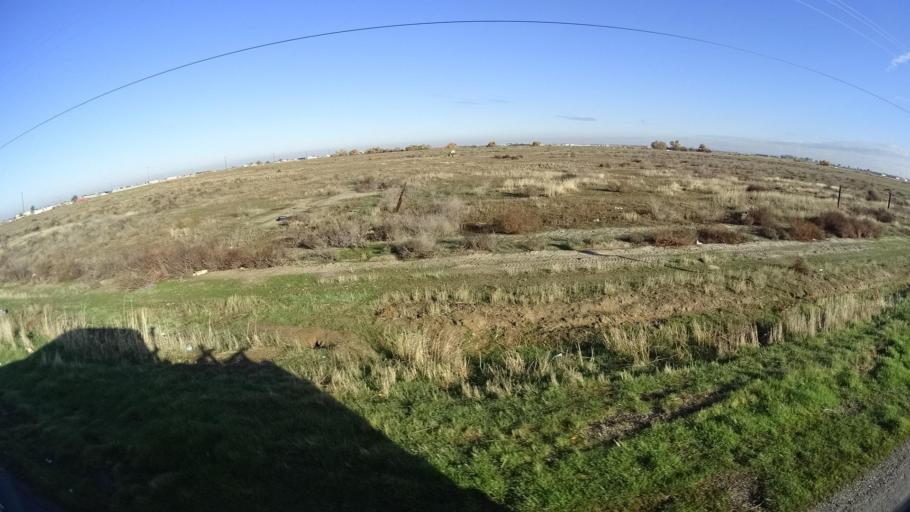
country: US
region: California
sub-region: Kern County
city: Delano
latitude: 35.7761
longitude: -119.3284
